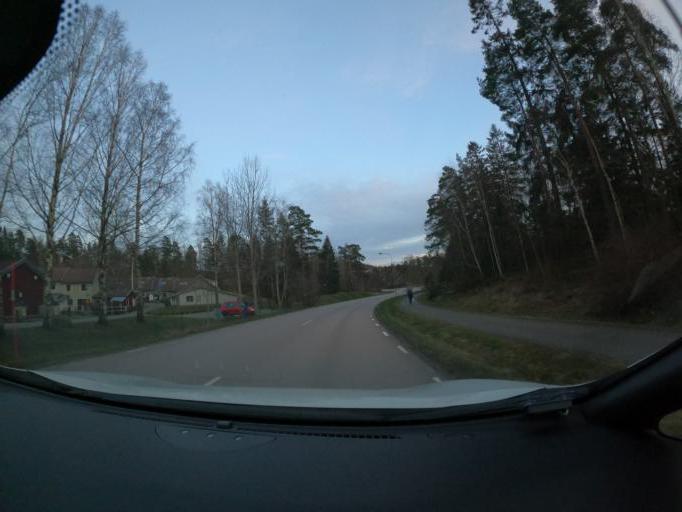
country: SE
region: Vaestra Goetaland
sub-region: Harryda Kommun
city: Molnlycke
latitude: 57.6509
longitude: 12.1410
